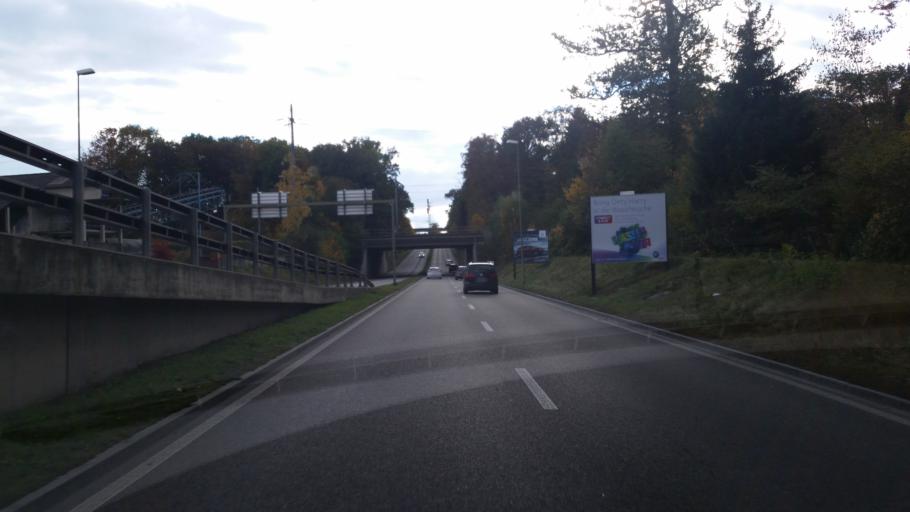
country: CH
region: Zurich
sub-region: Bezirk Buelach
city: Glattbrugg
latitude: 47.4353
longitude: 8.5540
